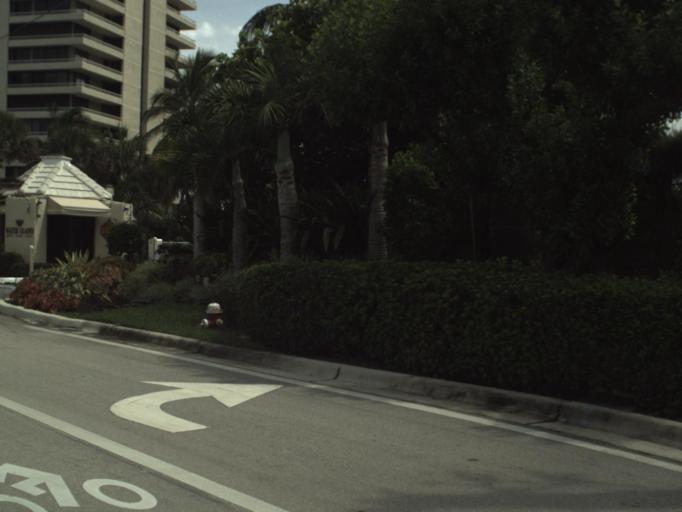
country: US
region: Florida
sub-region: Palm Beach County
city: Lake Park
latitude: 26.8125
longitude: -80.0364
